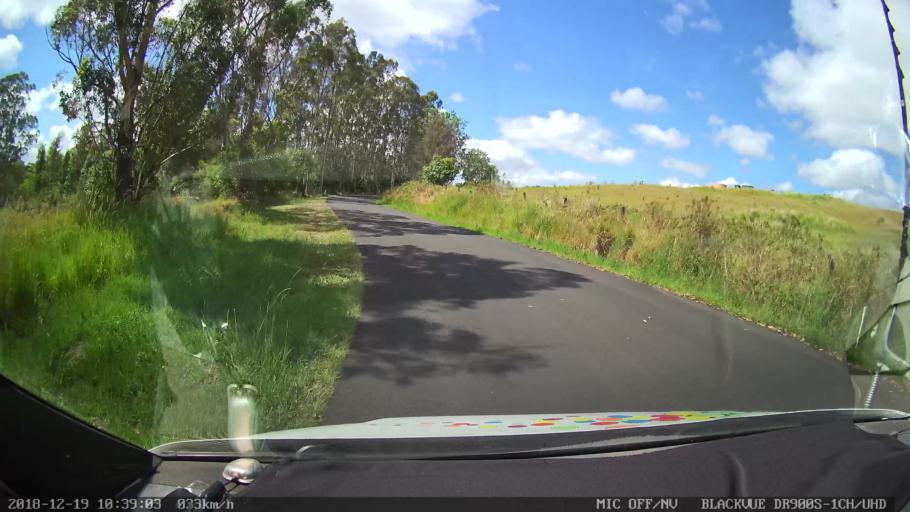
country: AU
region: New South Wales
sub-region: Lismore Municipality
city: Nimbin
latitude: -28.5782
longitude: 153.1544
